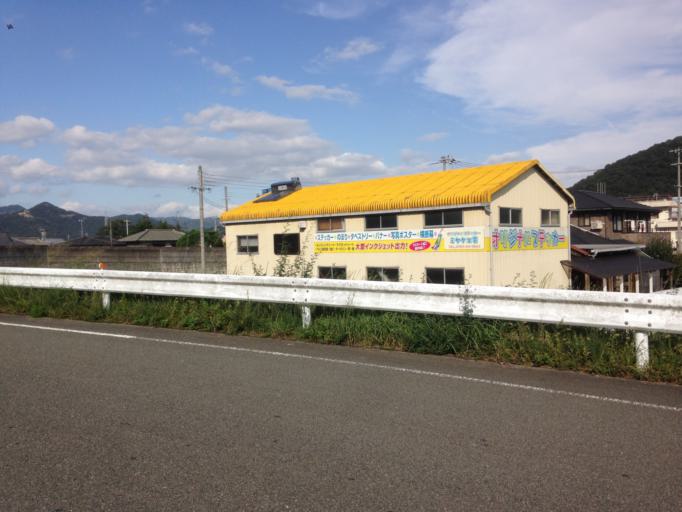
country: JP
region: Hyogo
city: Tatsunocho-tominaga
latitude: 34.8745
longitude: 134.5512
